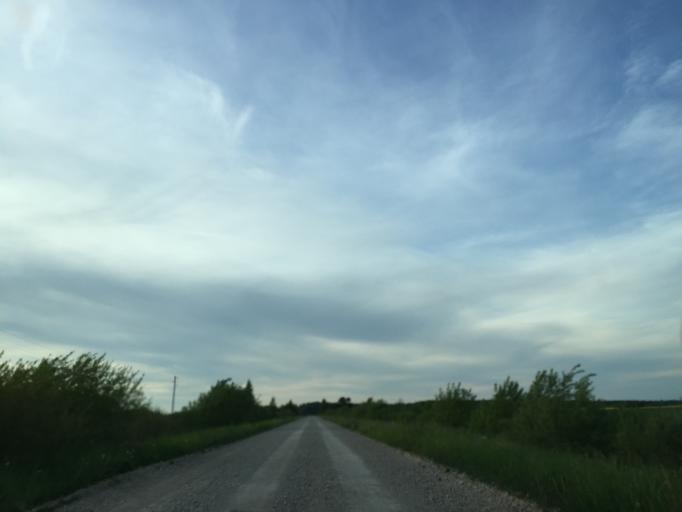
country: LV
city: Tireli
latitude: 56.7261
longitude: 23.5037
